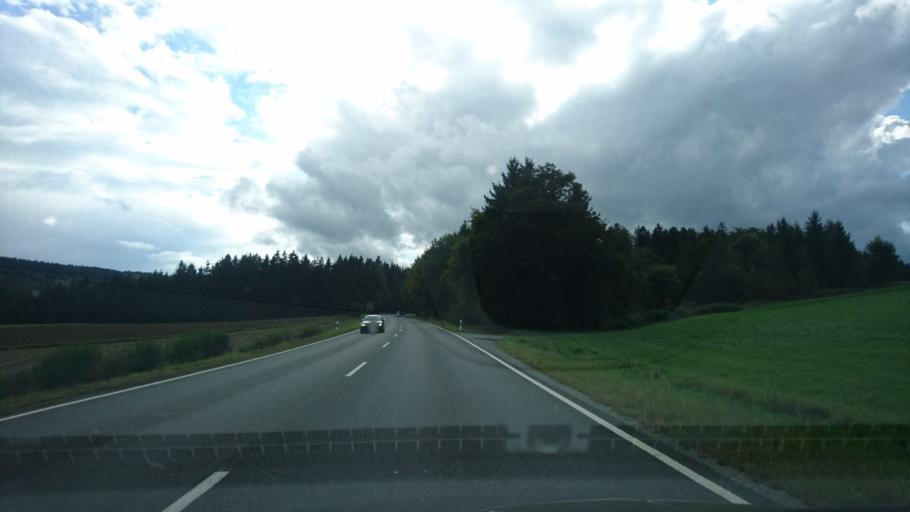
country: DE
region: Bavaria
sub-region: Upper Franconia
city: Naila
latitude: 50.2982
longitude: 11.6563
